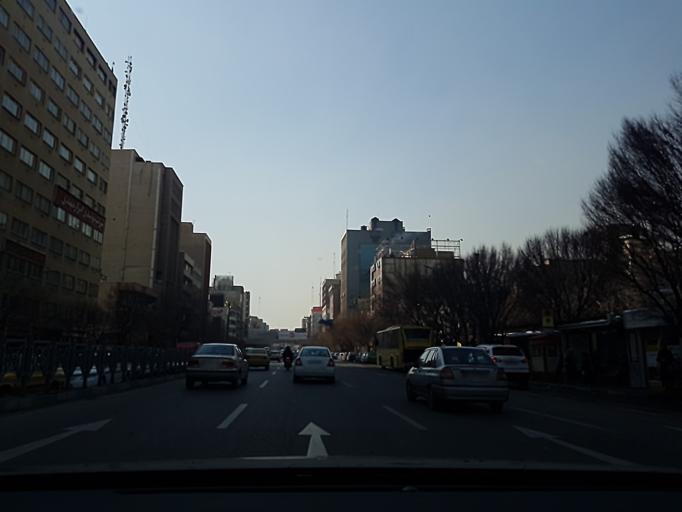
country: IR
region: Tehran
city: Tehran
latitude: 35.7153
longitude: 51.4241
